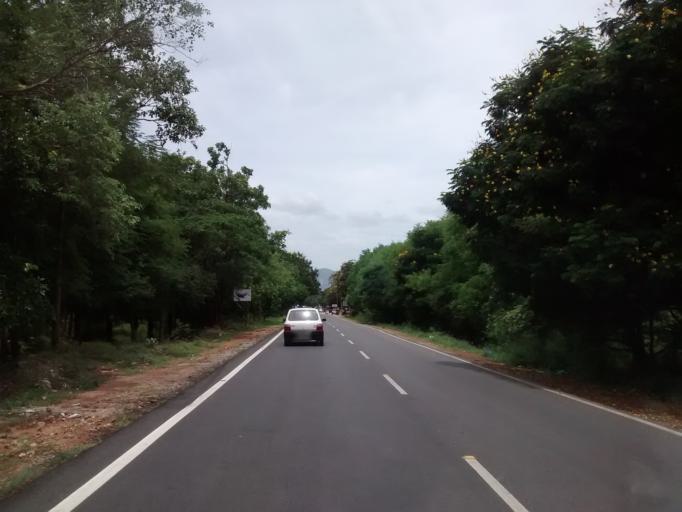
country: IN
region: Andhra Pradesh
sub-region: Chittoor
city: Narasingapuram
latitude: 13.6259
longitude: 79.3669
